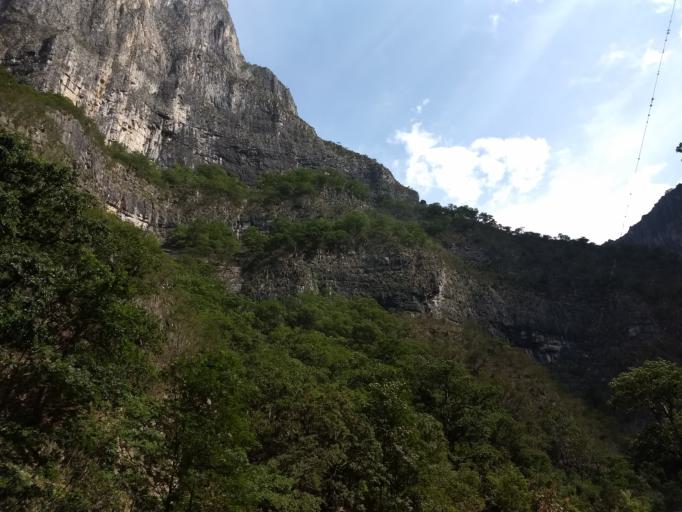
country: MX
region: Nuevo Leon
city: Santiago
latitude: 25.3810
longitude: -100.3091
